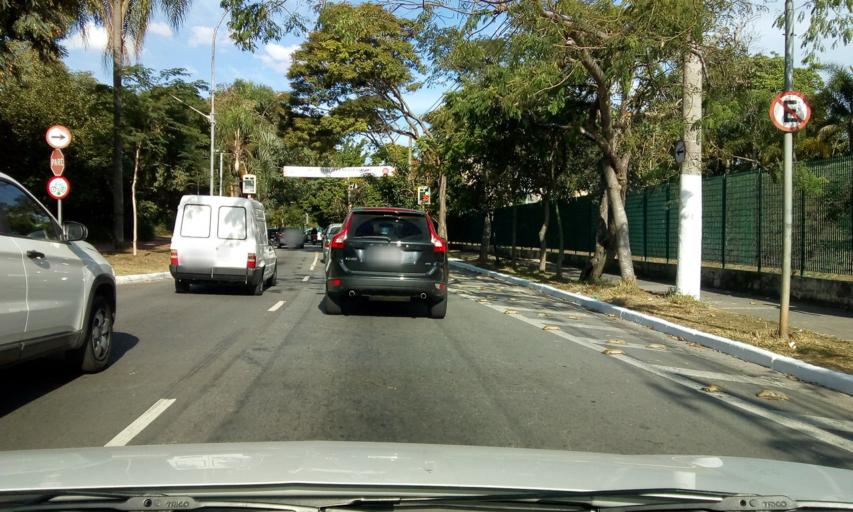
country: BR
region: Sao Paulo
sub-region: Osasco
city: Osasco
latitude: -23.5427
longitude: -46.7270
